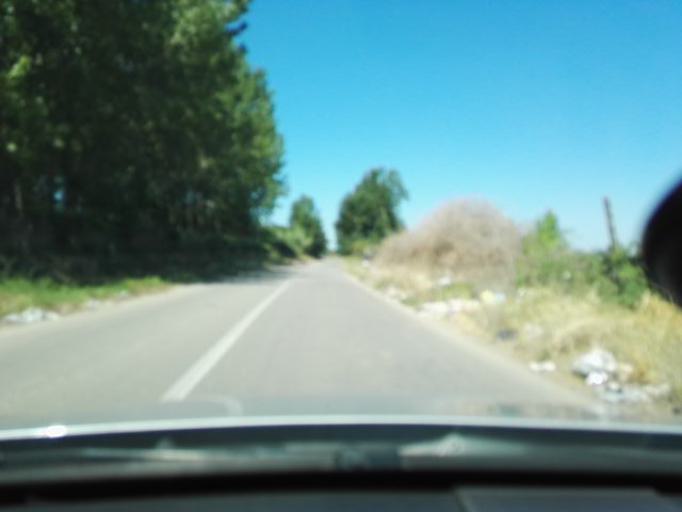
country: IT
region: Campania
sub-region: Provincia di Caserta
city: Villa di Briano
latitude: 40.9854
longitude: 14.1546
